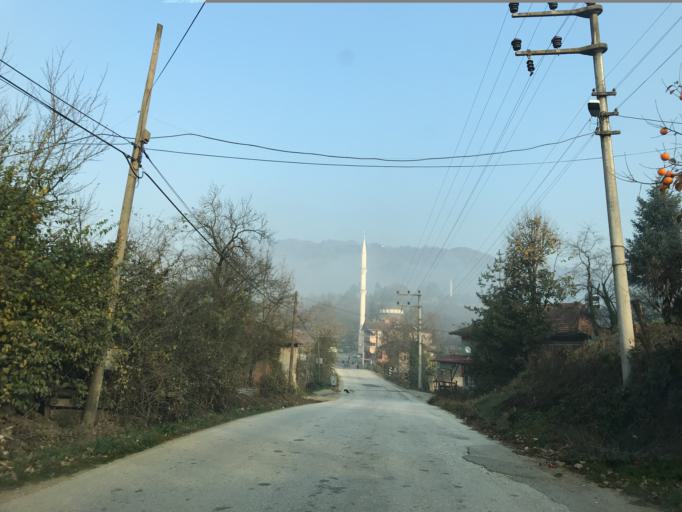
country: TR
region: Duzce
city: Cumayeri
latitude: 40.9061
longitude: 30.9513
